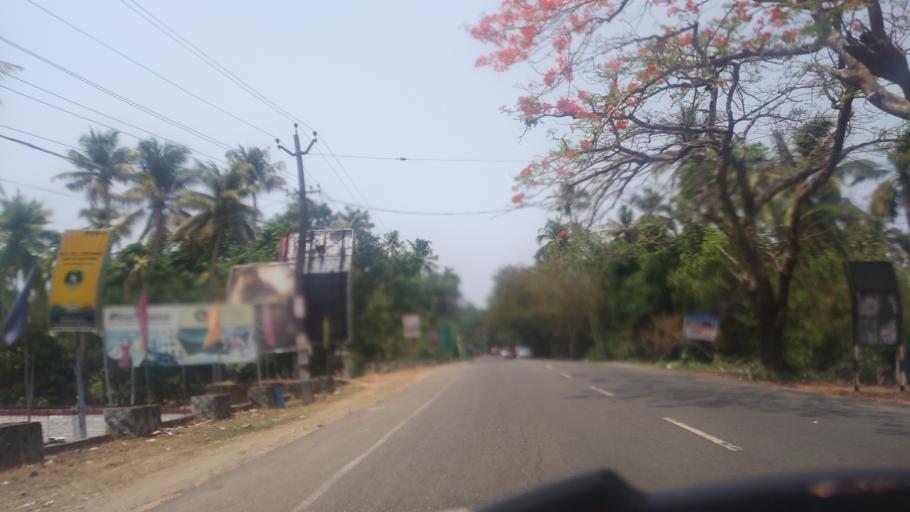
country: IN
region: Kerala
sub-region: Thrissur District
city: Kodungallur
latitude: 10.2618
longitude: 76.1820
